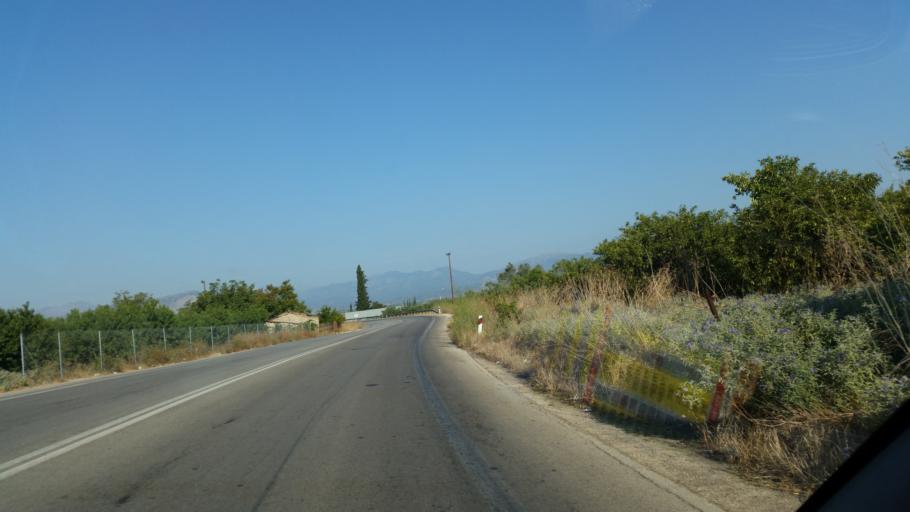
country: GR
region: Peloponnese
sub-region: Nomos Argolidos
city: Nea Tirins
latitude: 37.6121
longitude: 22.8235
